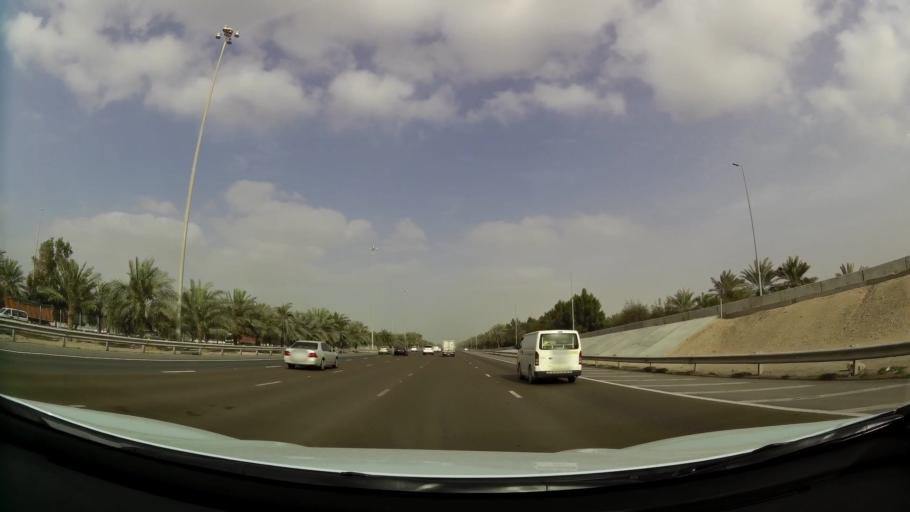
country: AE
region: Abu Dhabi
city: Abu Dhabi
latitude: 24.4275
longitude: 54.5384
